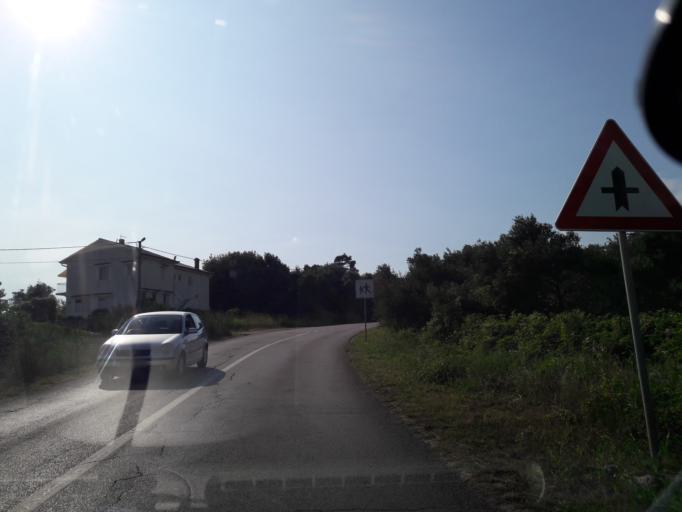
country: HR
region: Primorsko-Goranska
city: Banjol
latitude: 44.7529
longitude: 14.7802
